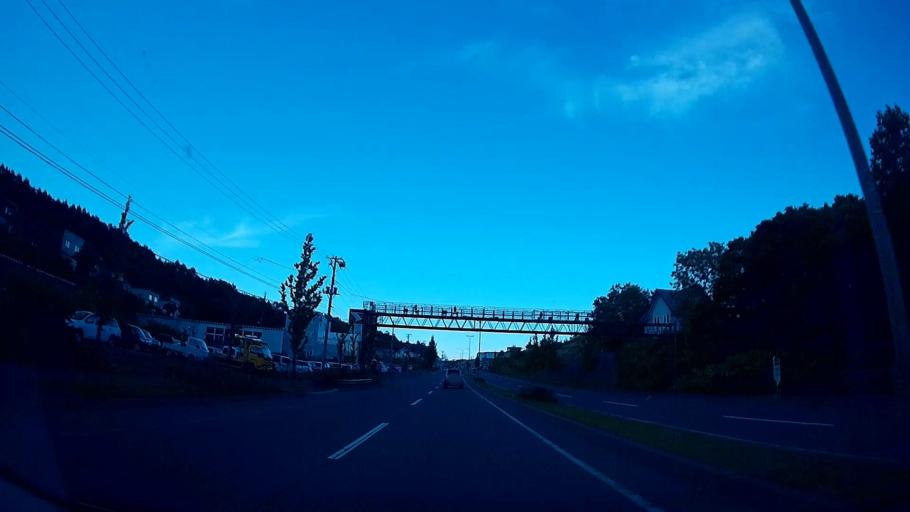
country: JP
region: Hokkaido
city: Otaru
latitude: 43.2117
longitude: 140.9355
